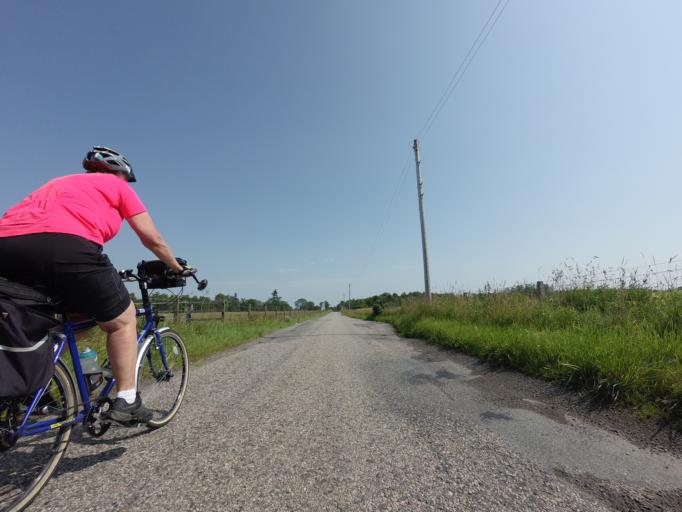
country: GB
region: Scotland
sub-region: Highland
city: Tain
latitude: 57.7946
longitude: -4.0769
